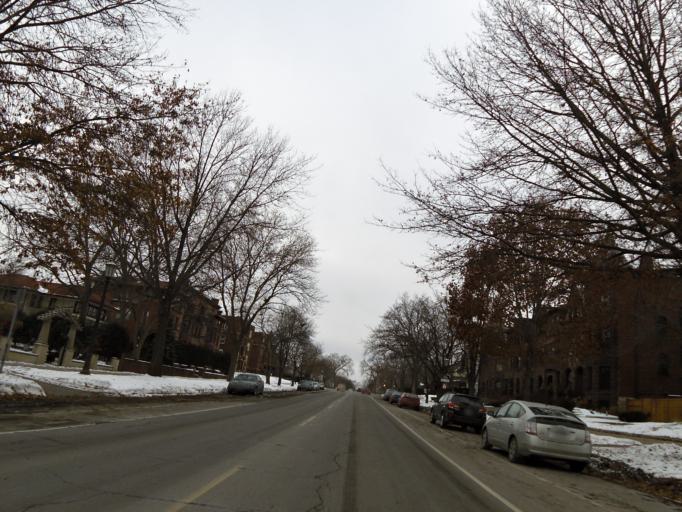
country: US
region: Minnesota
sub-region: Ramsey County
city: Saint Paul
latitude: 44.9414
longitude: -93.1243
